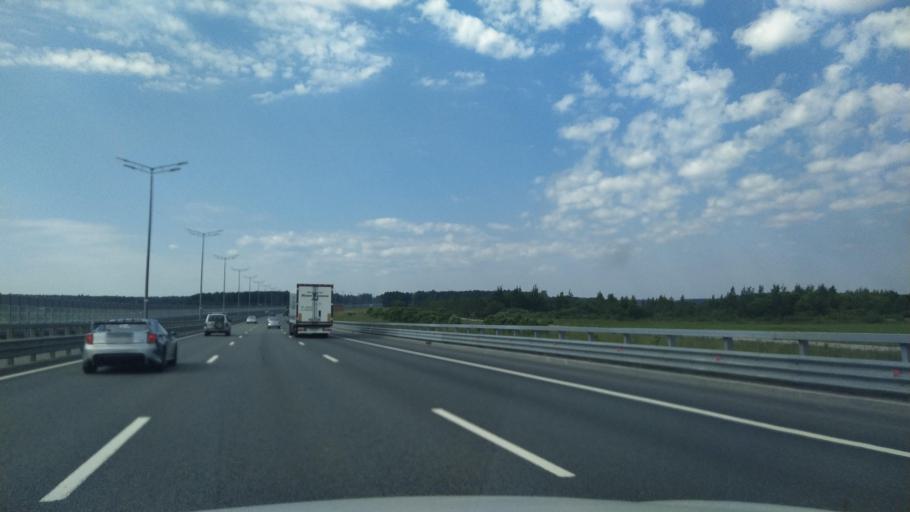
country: RU
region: St.-Petersburg
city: Levashovo
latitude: 60.0885
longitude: 30.2383
